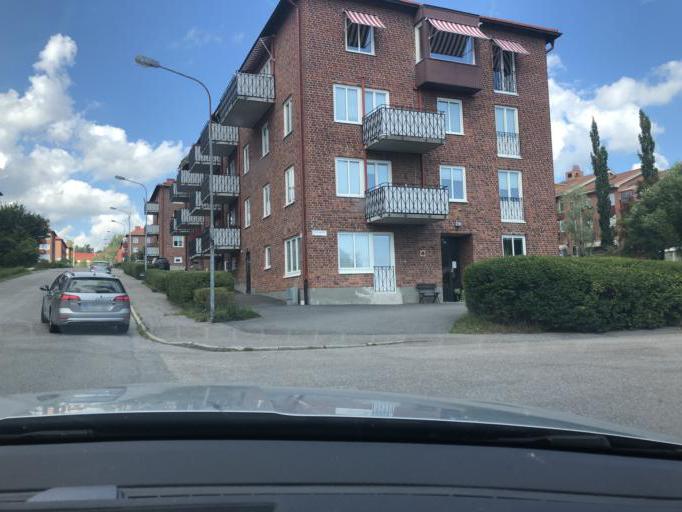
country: SE
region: Vaesternorrland
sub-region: Sundsvalls Kommun
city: Sundsvall
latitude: 62.3987
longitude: 17.3211
